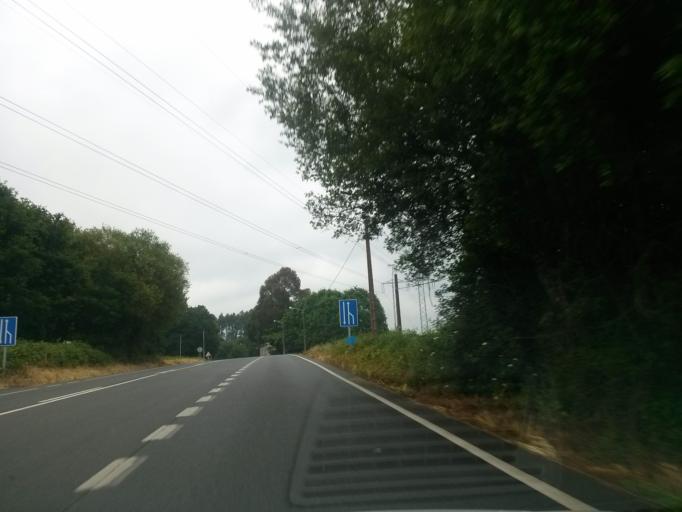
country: ES
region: Galicia
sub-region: Provincia de Lugo
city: Begonte
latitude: 43.1462
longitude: -7.6807
